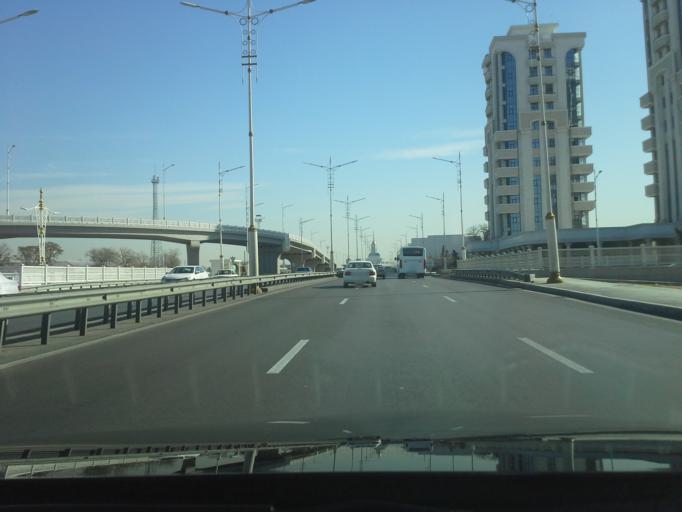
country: TM
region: Ahal
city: Ashgabat
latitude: 37.9475
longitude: 58.3871
